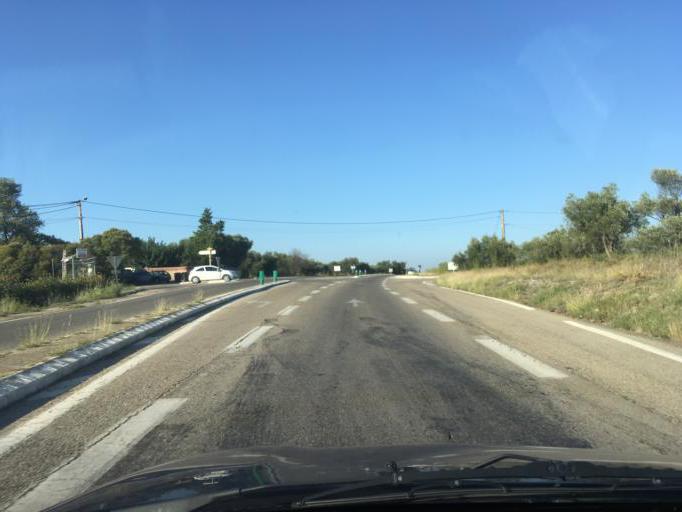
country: FR
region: Languedoc-Roussillon
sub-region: Departement du Gard
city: Ledenon
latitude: 43.9088
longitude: 4.5229
